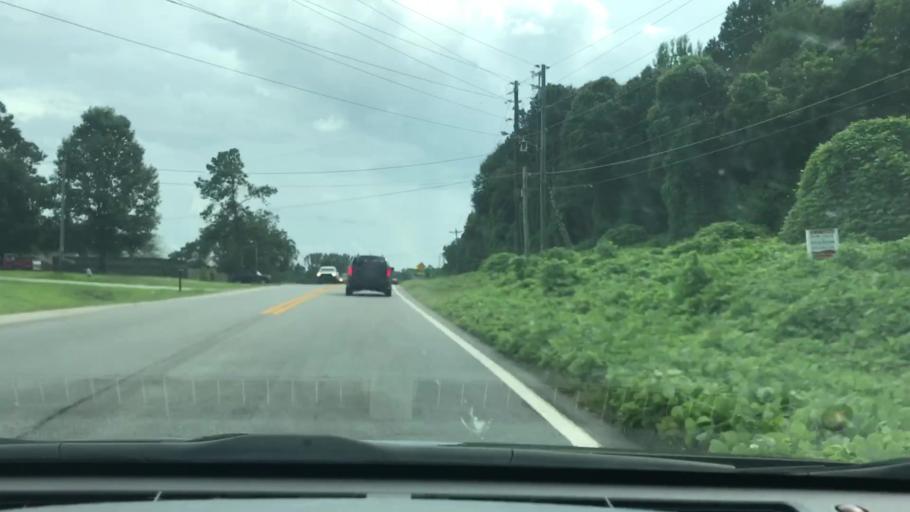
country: US
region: Georgia
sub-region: Walton County
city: Walnut Grove
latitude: 33.7607
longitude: -83.8512
